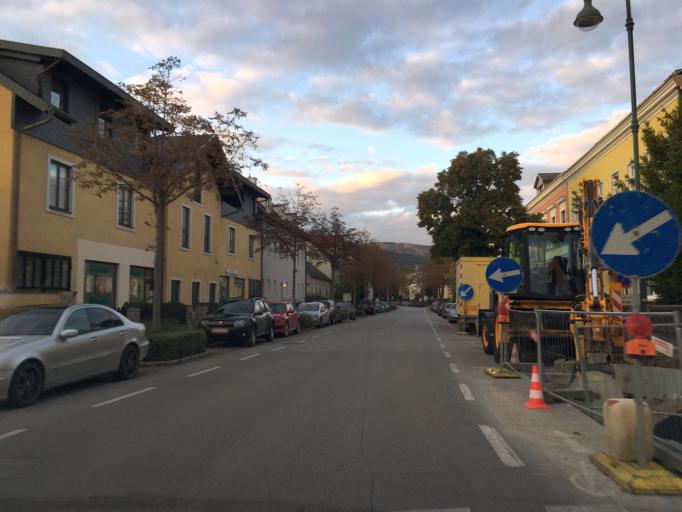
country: AT
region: Lower Austria
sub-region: Politischer Bezirk Baden
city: Baden
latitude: 48.0075
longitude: 16.2441
